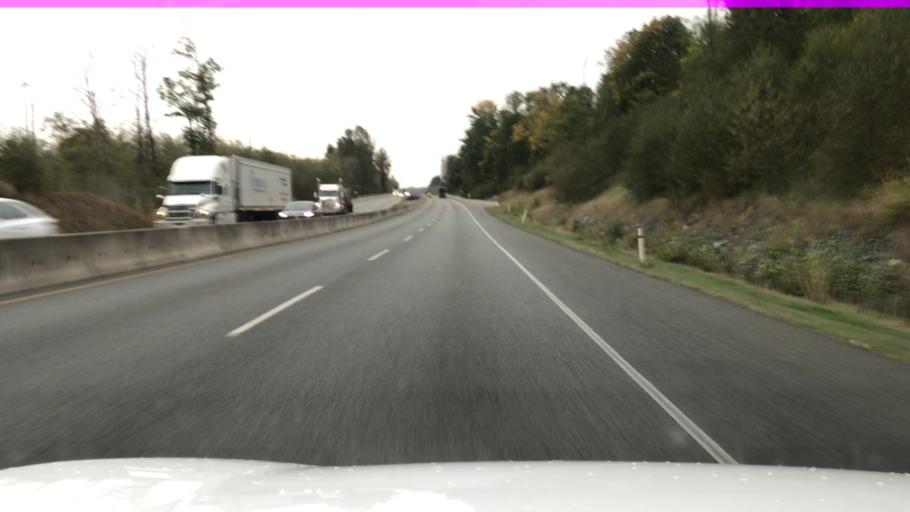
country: CA
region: British Columbia
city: Pitt Meadows
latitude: 49.2057
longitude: -122.7622
